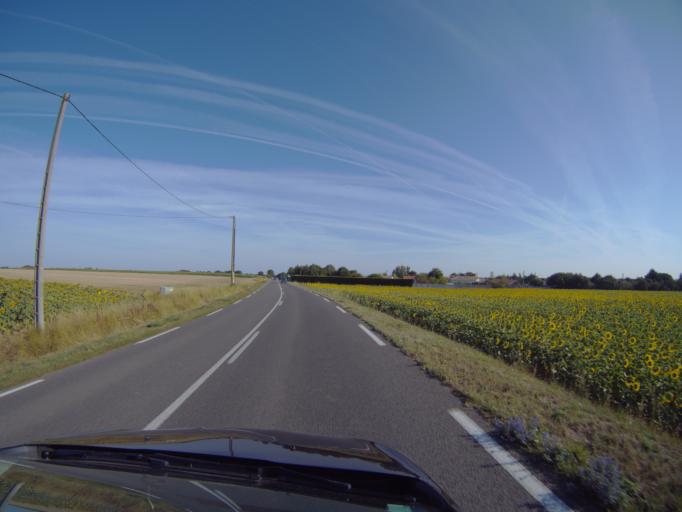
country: FR
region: Pays de la Loire
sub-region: Departement de la Vendee
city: Jard-sur-Mer
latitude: 46.4425
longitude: -1.5786
